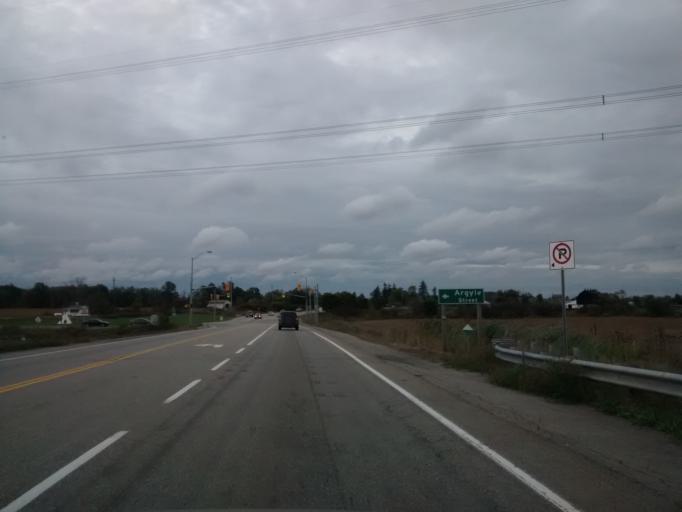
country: CA
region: Ontario
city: Ancaster
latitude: 43.0508
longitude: -79.9744
